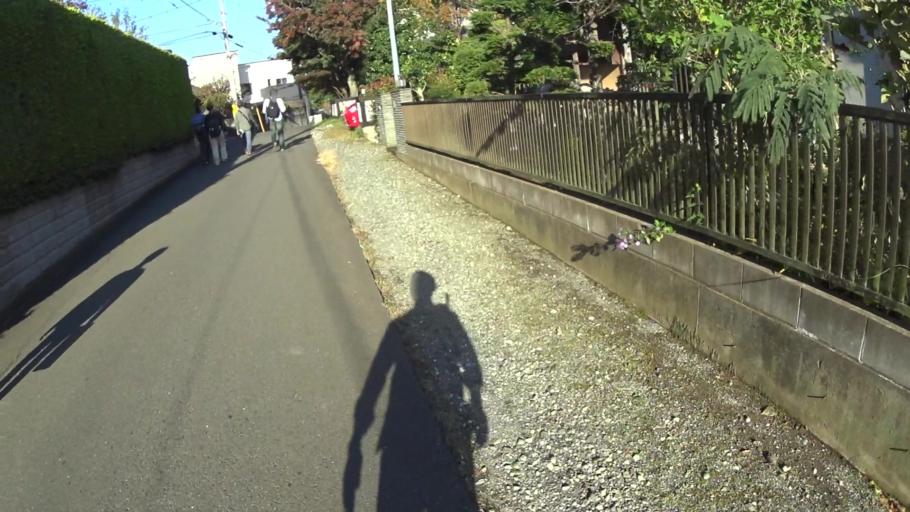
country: JP
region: Tokyo
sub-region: Machida-shi
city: Machida
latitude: 35.5786
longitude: 139.4450
